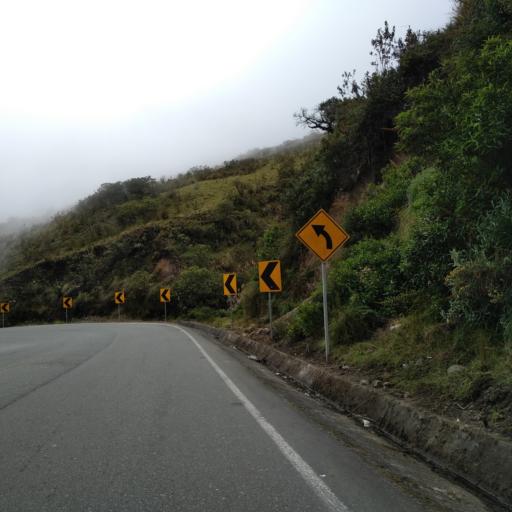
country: EC
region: Cotopaxi
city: La Mana
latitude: -0.9875
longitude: -78.9687
